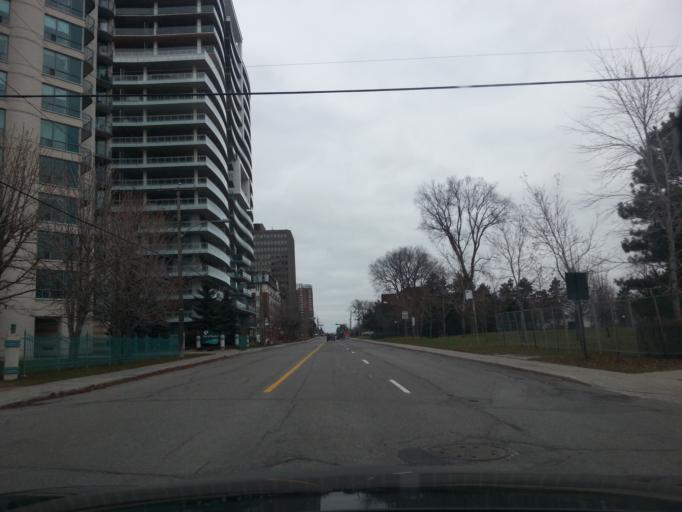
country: CA
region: Ontario
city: Ottawa
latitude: 45.4344
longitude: -75.7092
